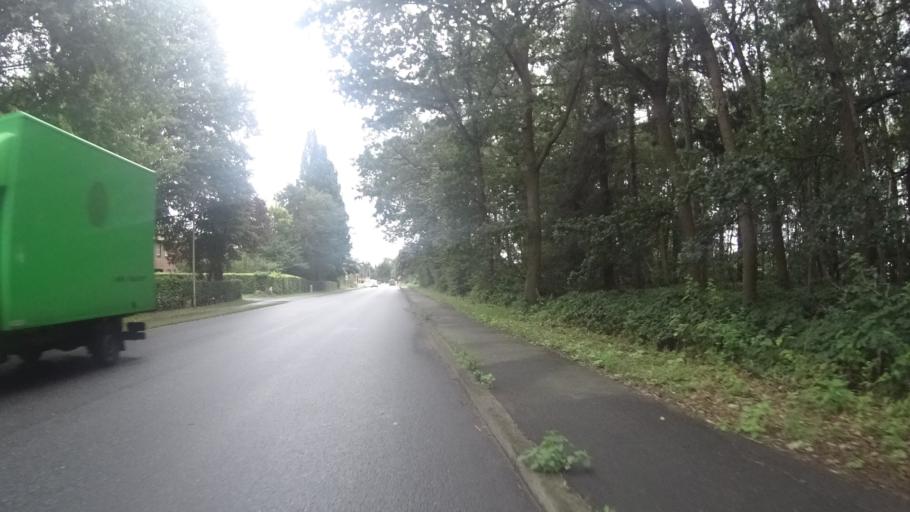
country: DE
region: Schleswig-Holstein
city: Kiebitzreihe
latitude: 53.7843
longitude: 9.6368
